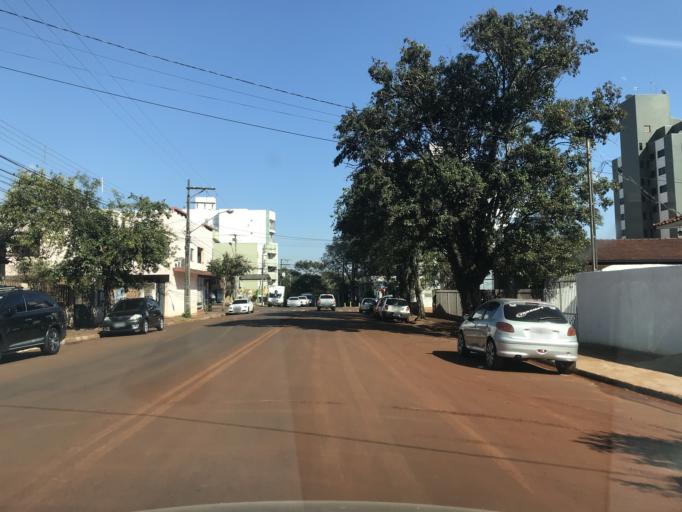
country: BR
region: Parana
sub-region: Toledo
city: Toledo
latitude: -24.7237
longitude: -53.7411
